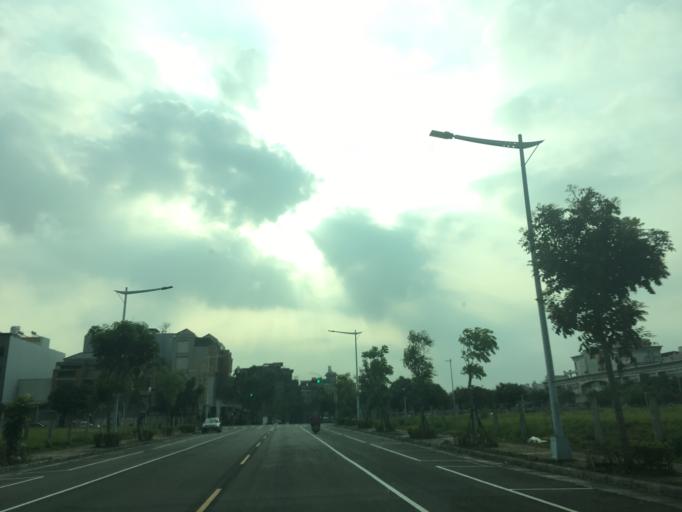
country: TW
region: Taiwan
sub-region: Taichung City
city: Taichung
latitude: 24.1954
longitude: 120.6750
